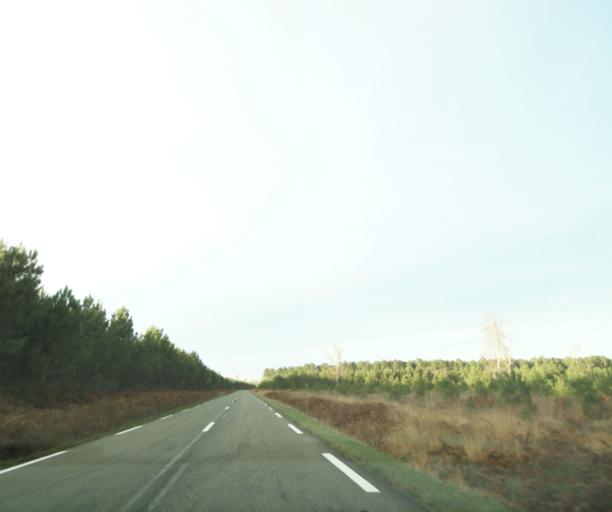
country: FR
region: Aquitaine
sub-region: Departement des Landes
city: Gabarret
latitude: 44.0880
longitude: -0.0946
